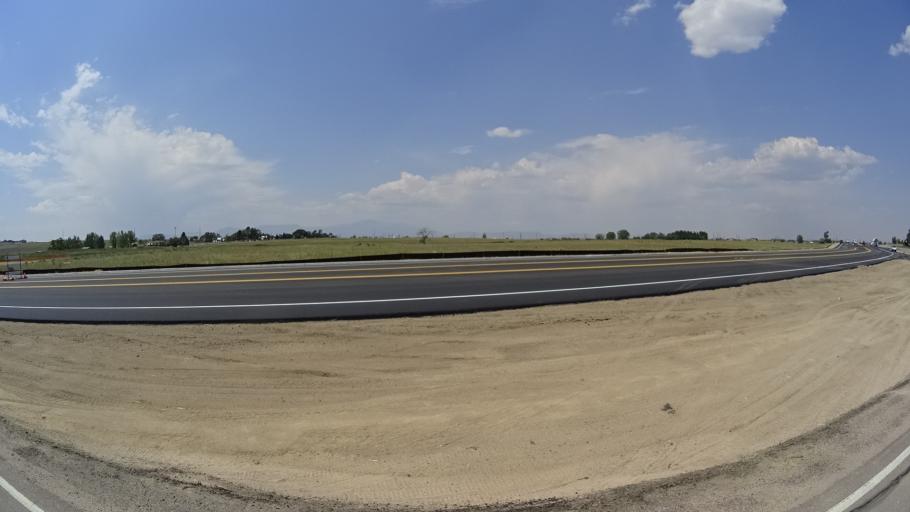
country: US
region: Colorado
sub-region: El Paso County
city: Cimarron Hills
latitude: 38.9283
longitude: -104.6079
